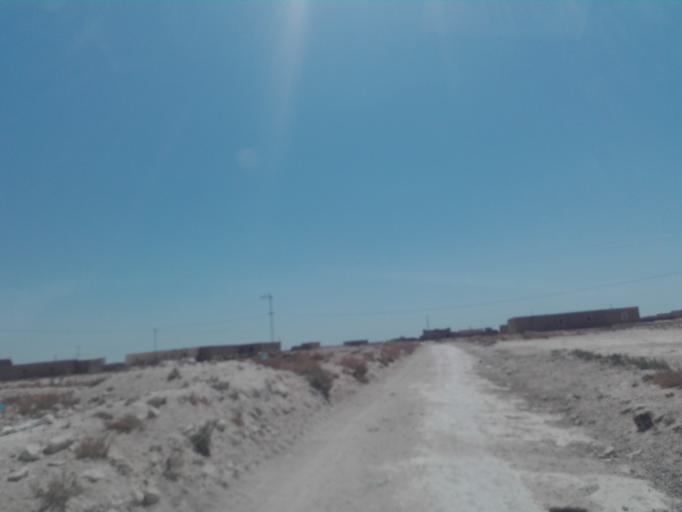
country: TN
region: Safaqis
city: Skhira
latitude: 34.3784
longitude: 9.9239
